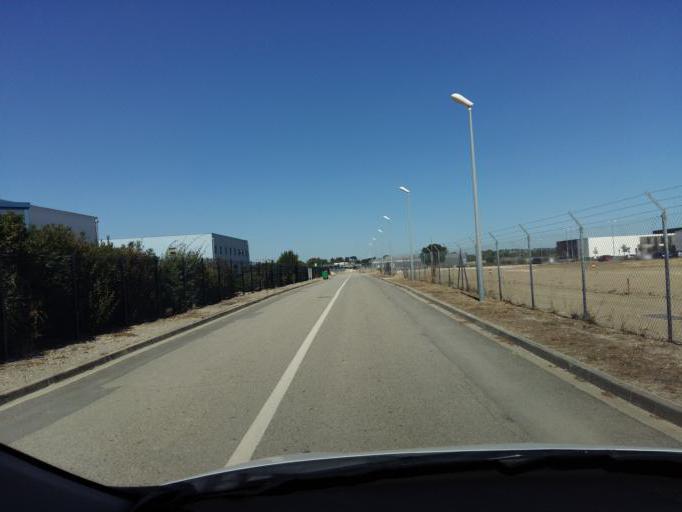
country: FR
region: Provence-Alpes-Cote d'Azur
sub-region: Departement des Bouches-du-Rhone
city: Noves
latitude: 43.9080
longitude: 4.8966
